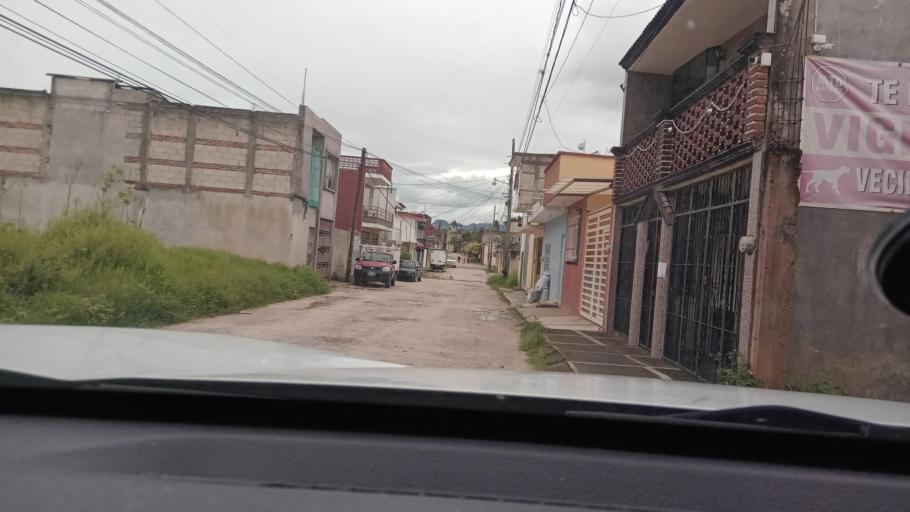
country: MX
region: Veracruz
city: Coatepec
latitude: 19.4428
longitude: -96.9699
